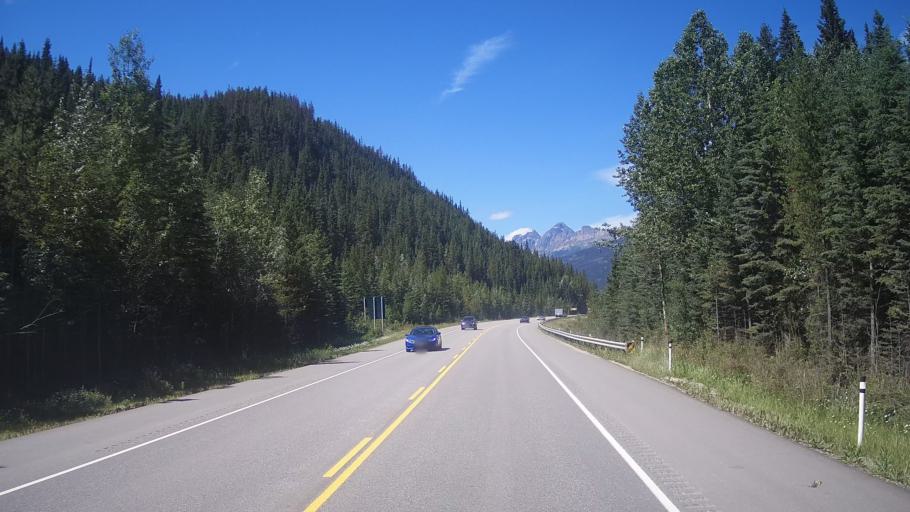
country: CA
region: Alberta
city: Jasper Park Lodge
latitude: 52.8822
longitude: -118.4152
